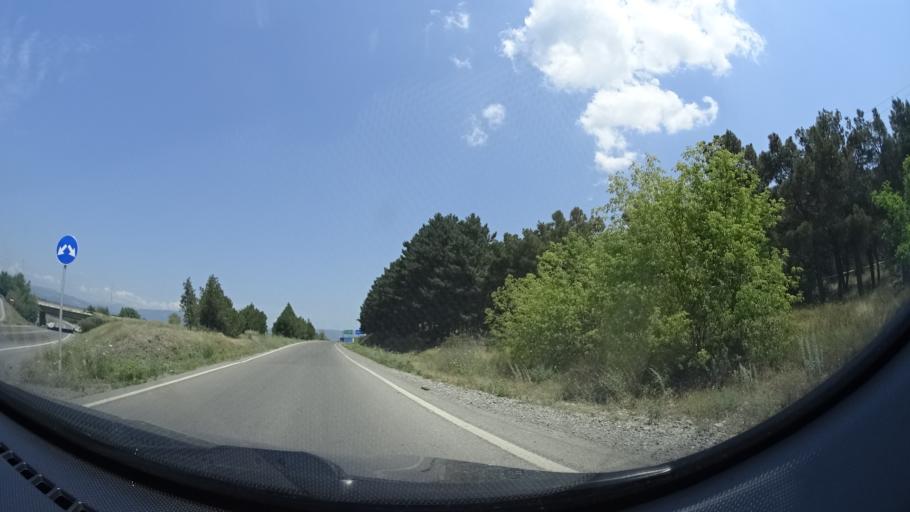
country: GE
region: Shida Kartli
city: Gori
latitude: 42.0149
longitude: 44.1389
